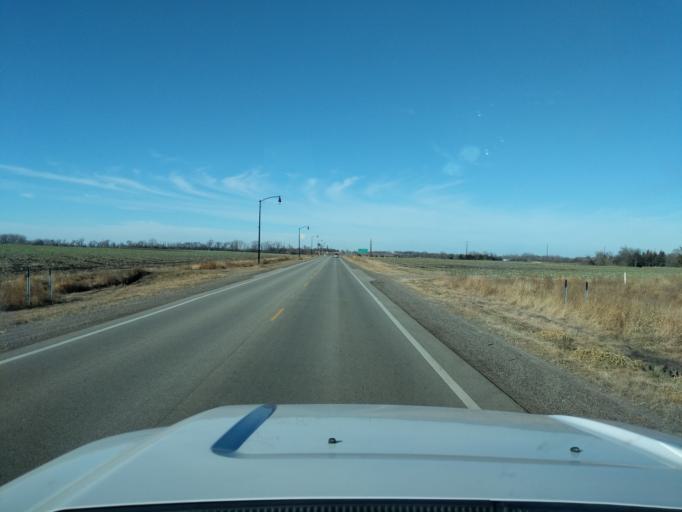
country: US
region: Minnesota
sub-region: Yellow Medicine County
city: Granite Falls
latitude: 44.7683
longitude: -95.5387
